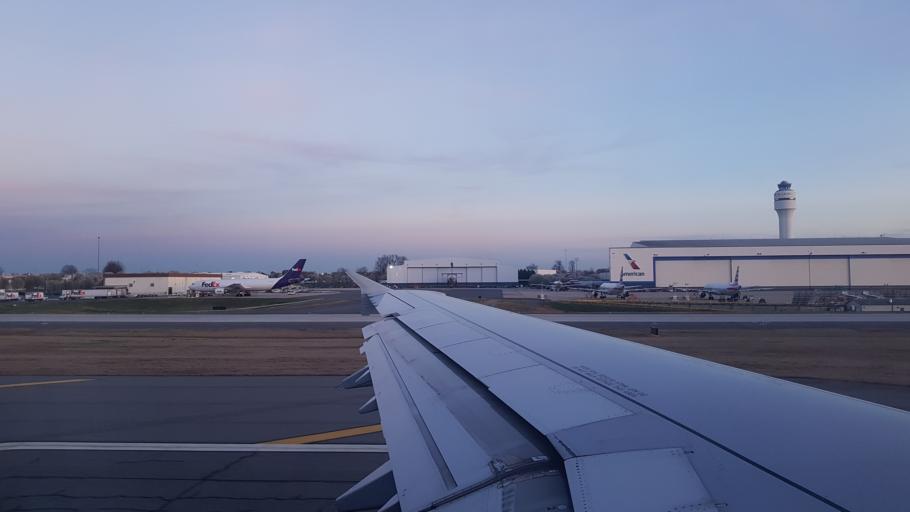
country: US
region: North Carolina
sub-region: Gaston County
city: Belmont
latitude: 35.2114
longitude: -80.9465
